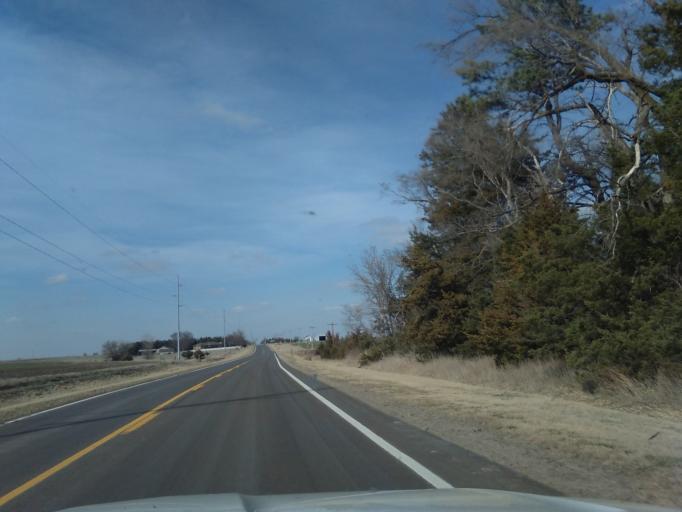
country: US
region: Nebraska
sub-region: Gage County
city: Beatrice
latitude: 40.2025
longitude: -96.9354
